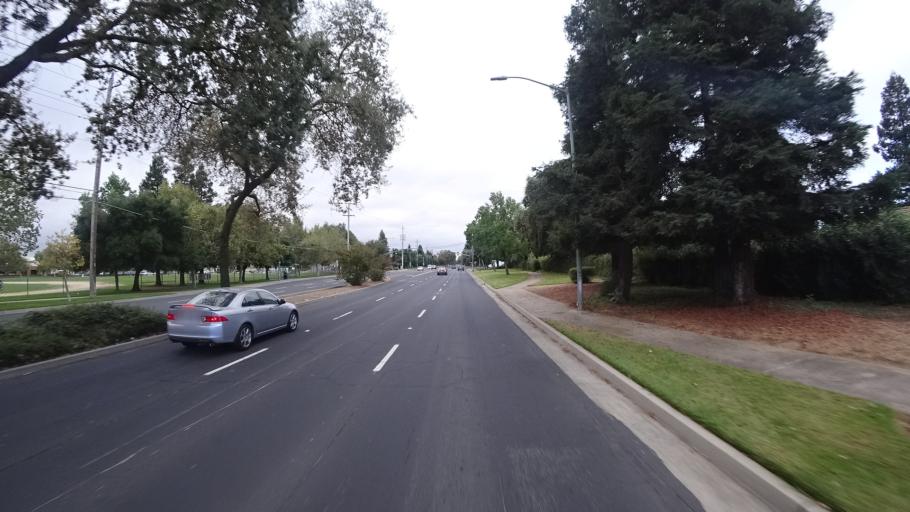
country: US
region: California
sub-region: Sacramento County
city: Laguna
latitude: 38.4202
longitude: -121.4180
